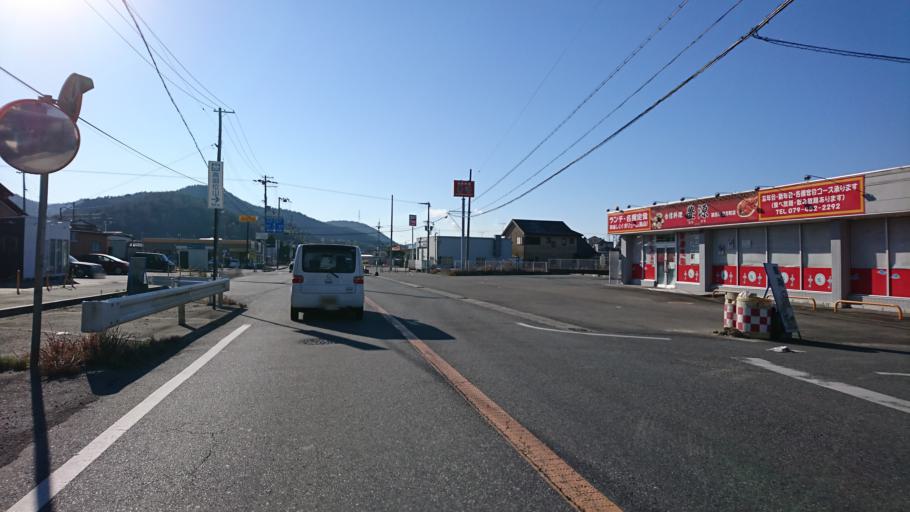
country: JP
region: Hyogo
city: Kakogawacho-honmachi
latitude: 34.8160
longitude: 134.8354
